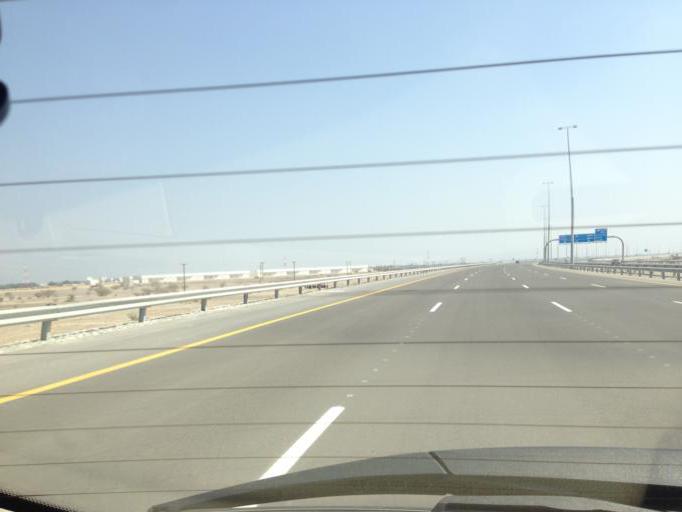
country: OM
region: Al Batinah
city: Barka'
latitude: 23.6265
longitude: 57.8476
